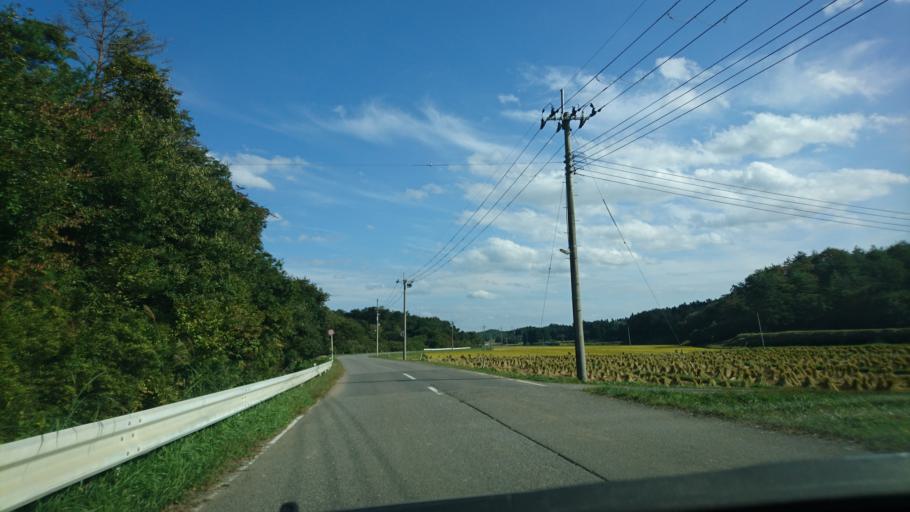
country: JP
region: Iwate
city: Ichinoseki
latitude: 38.8795
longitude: 141.0654
